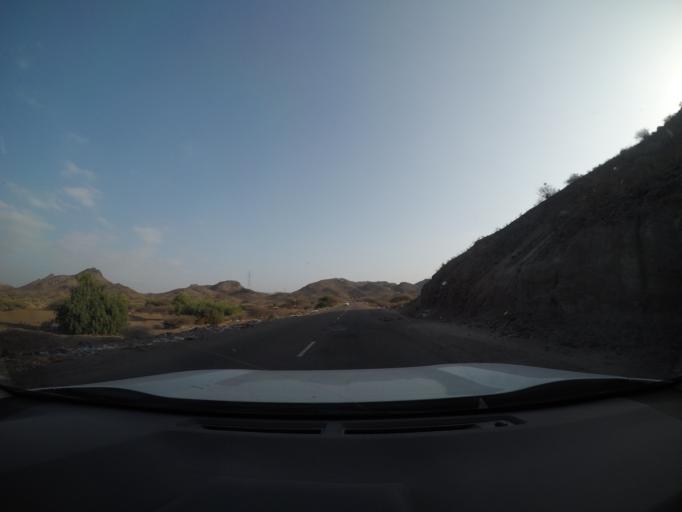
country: YE
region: Lahij
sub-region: Al Milah
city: Al Milah
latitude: 13.3780
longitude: 44.8068
